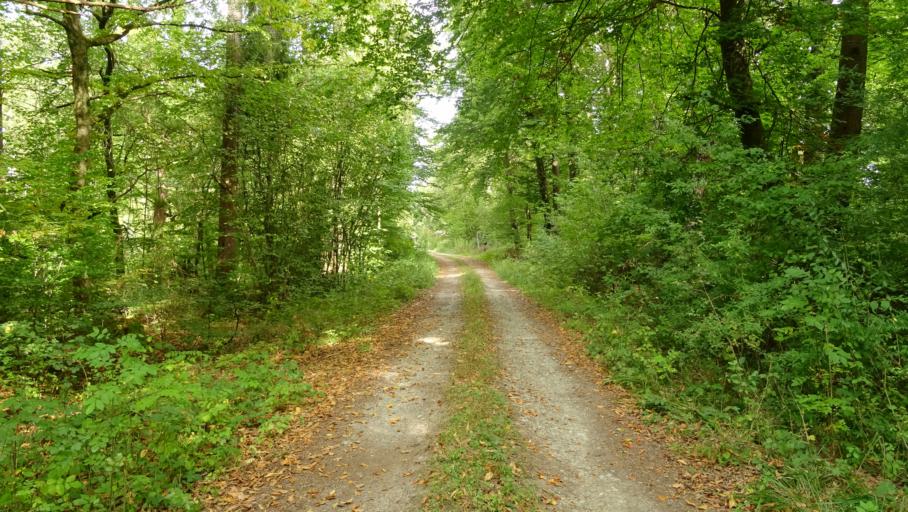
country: DE
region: Baden-Wuerttemberg
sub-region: Karlsruhe Region
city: Mosbach
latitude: 49.3901
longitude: 9.1584
